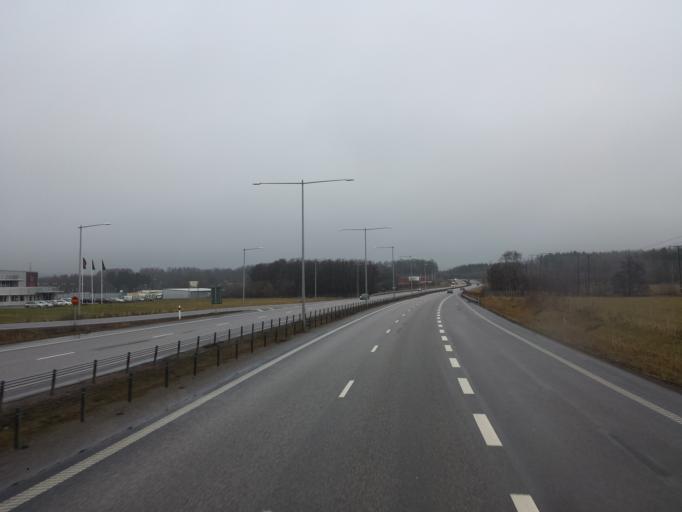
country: SE
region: OEstergoetland
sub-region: Norrkopings Kommun
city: Jursla
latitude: 58.6482
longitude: 16.1735
